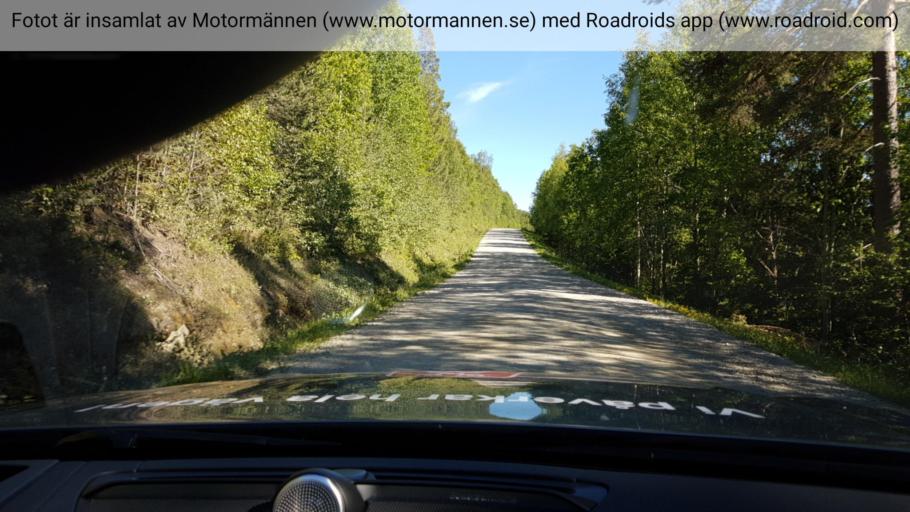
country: SE
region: Jaemtland
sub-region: Bergs Kommun
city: Hoverberg
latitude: 62.6940
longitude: 14.7238
